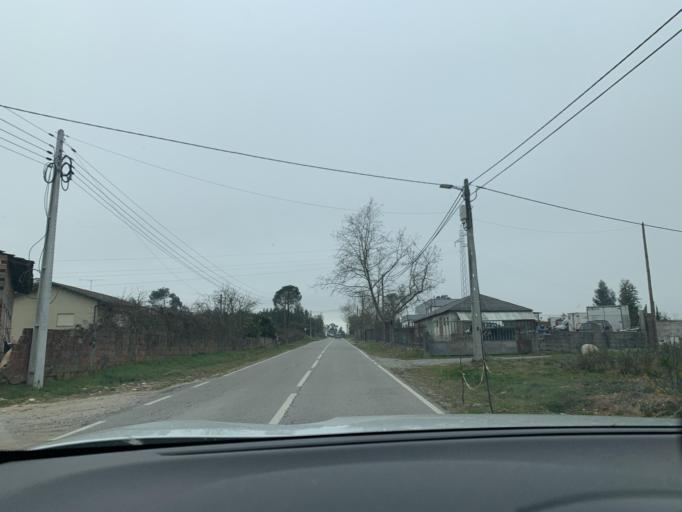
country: PT
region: Viseu
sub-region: Concelho de Tondela
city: Tondela
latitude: 40.5333
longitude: -8.0538
